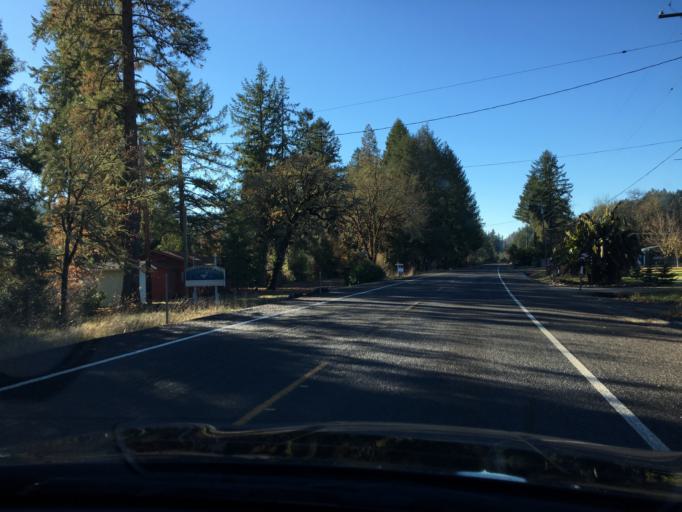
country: US
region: Oregon
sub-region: Douglas County
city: Glide
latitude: 43.3224
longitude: -123.0324
